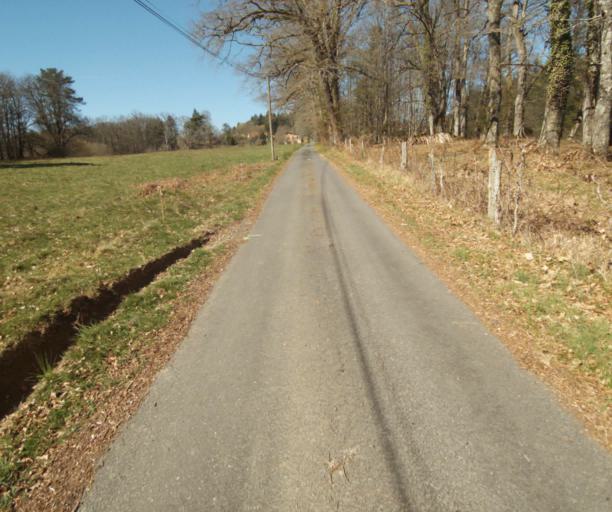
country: FR
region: Limousin
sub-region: Departement de la Correze
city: Saint-Mexant
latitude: 45.3037
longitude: 1.6273
